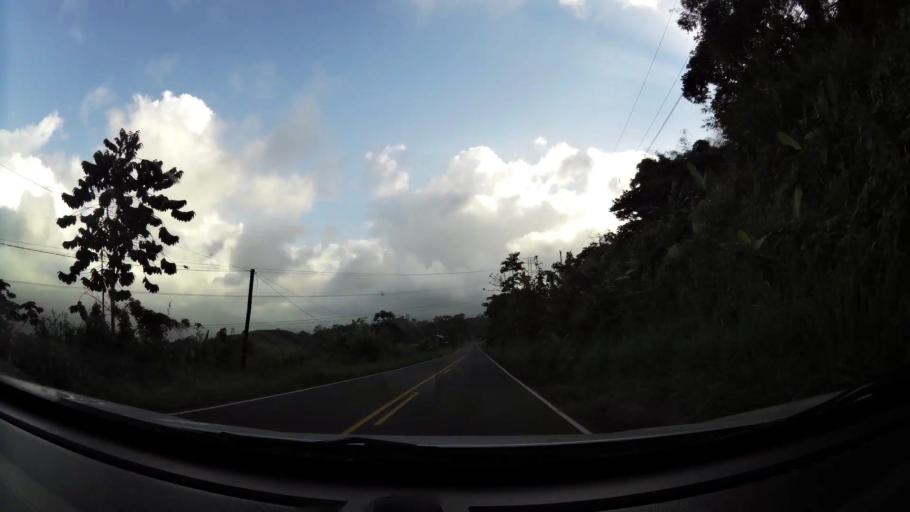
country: CR
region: Limon
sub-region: Canton de Siquirres
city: Siquirres
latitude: 10.0182
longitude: -83.5632
